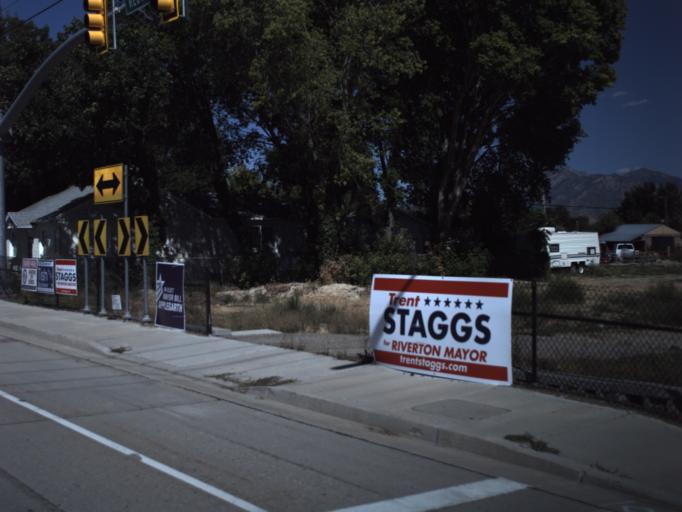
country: US
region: Utah
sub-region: Salt Lake County
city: Riverton
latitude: 40.5367
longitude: -111.9386
